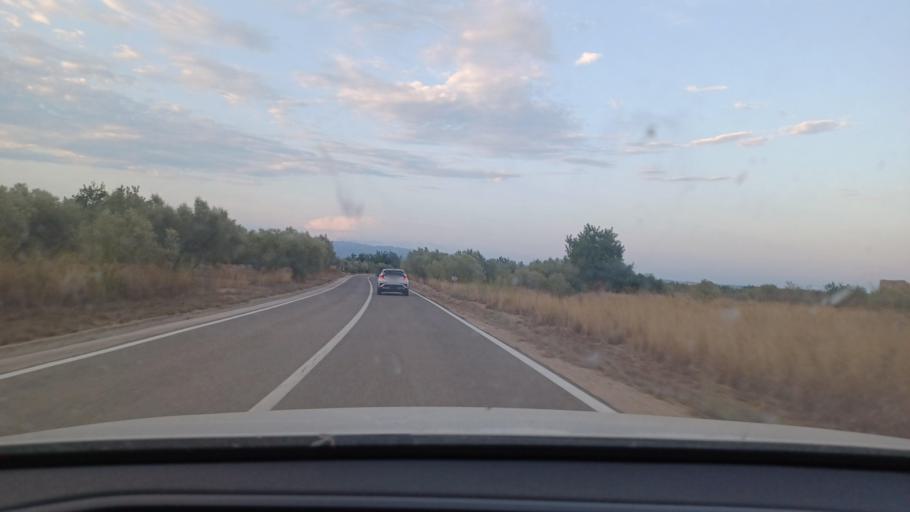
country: ES
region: Catalonia
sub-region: Provincia de Tarragona
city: Mas de Barberans
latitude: 40.7178
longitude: 0.4216
